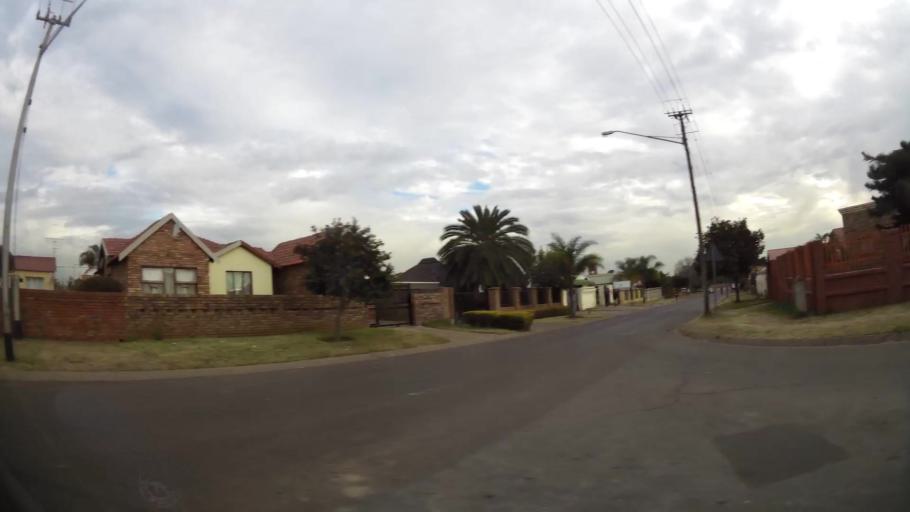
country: ZA
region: Gauteng
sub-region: City of Tshwane Metropolitan Municipality
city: Pretoria
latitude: -25.7049
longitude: 28.3118
